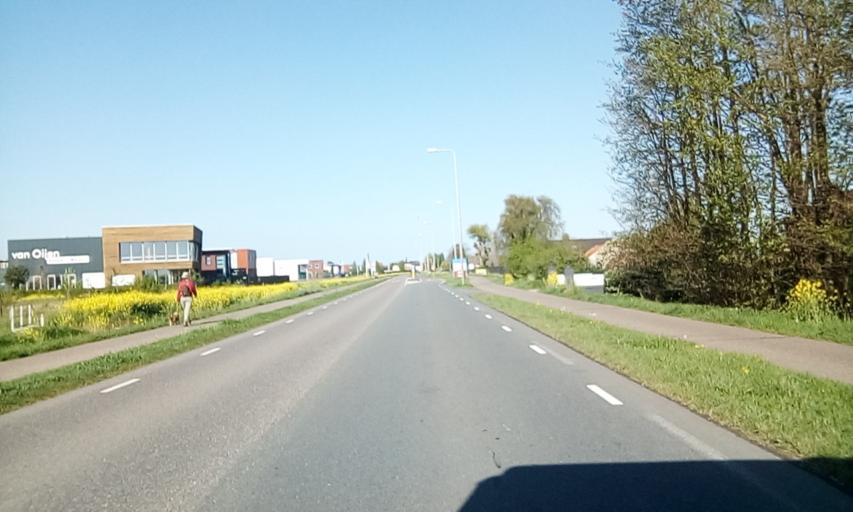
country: NL
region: Gelderland
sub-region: Gemeente Druten
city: Druten
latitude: 51.8794
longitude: 5.5409
